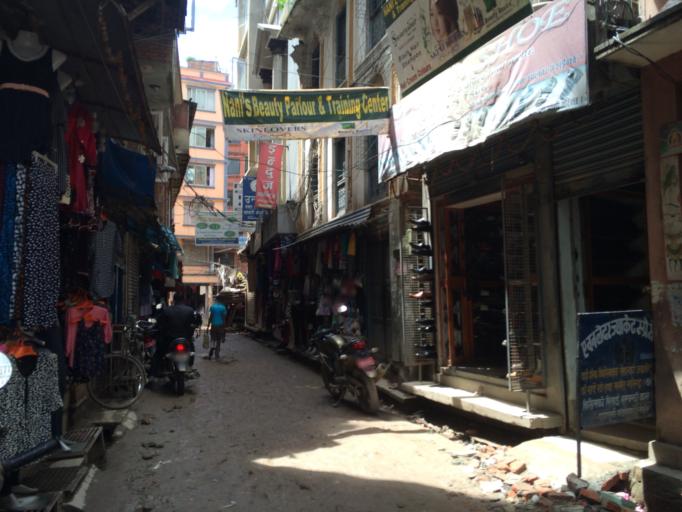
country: NP
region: Central Region
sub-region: Bagmati Zone
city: Kathmandu
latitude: 27.7098
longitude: 85.3109
